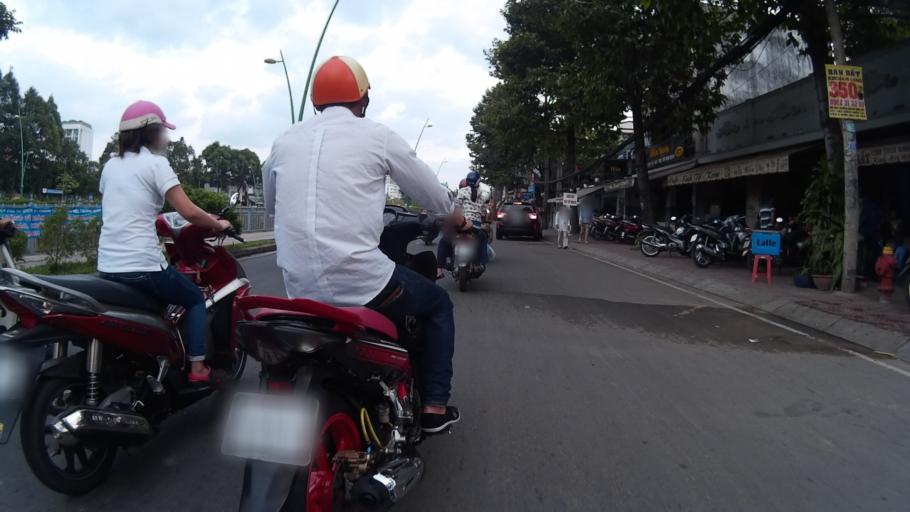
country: VN
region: Ho Chi Minh City
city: Quan Phu Nhuan
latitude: 10.7847
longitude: 106.6767
